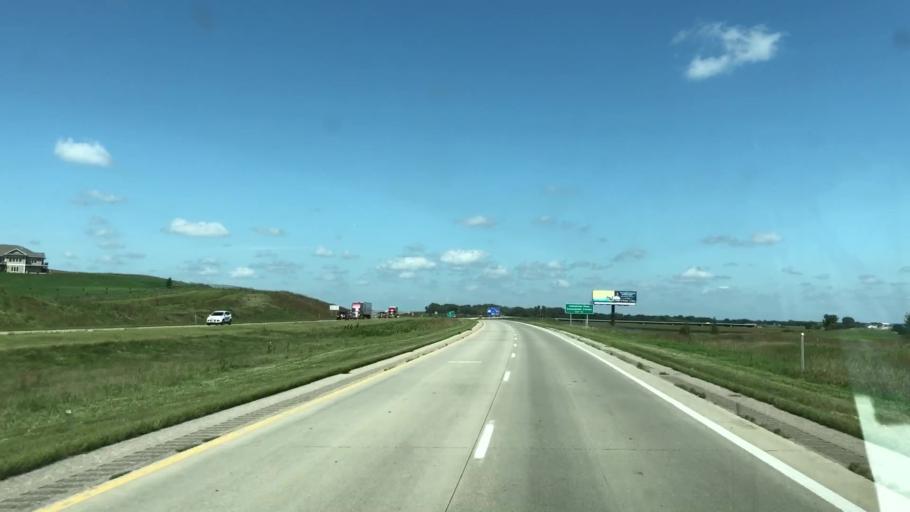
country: US
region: Iowa
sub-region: Plymouth County
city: Le Mars
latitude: 42.7530
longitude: -96.2098
